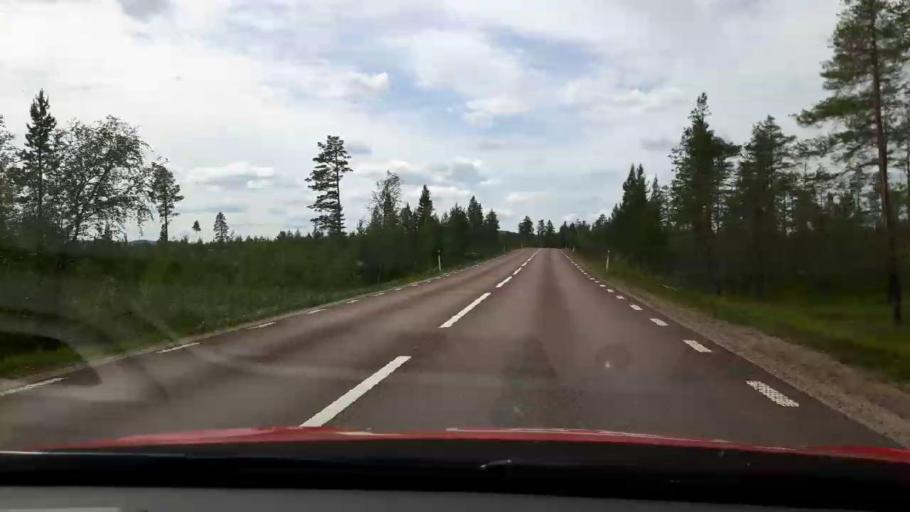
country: SE
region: Jaemtland
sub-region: Harjedalens Kommun
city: Sveg
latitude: 62.0411
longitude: 14.4636
